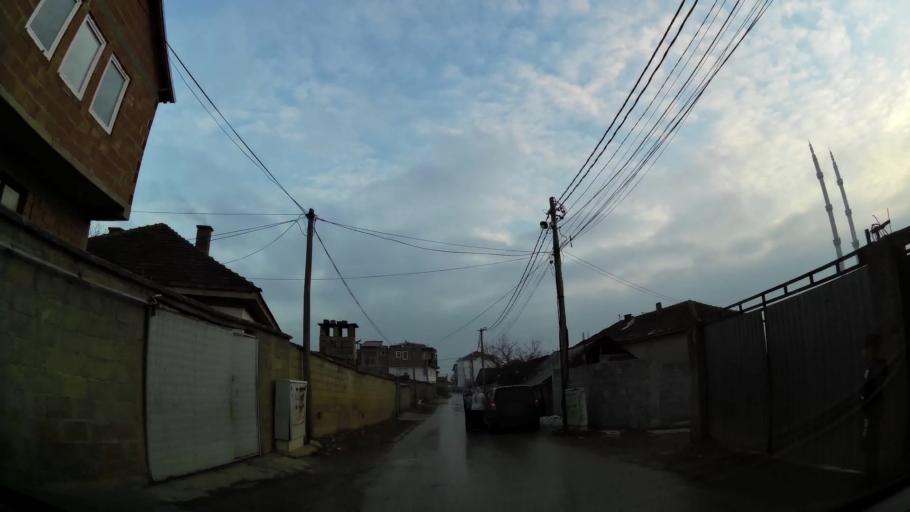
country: MK
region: Aracinovo
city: Arachinovo
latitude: 42.0299
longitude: 21.5590
